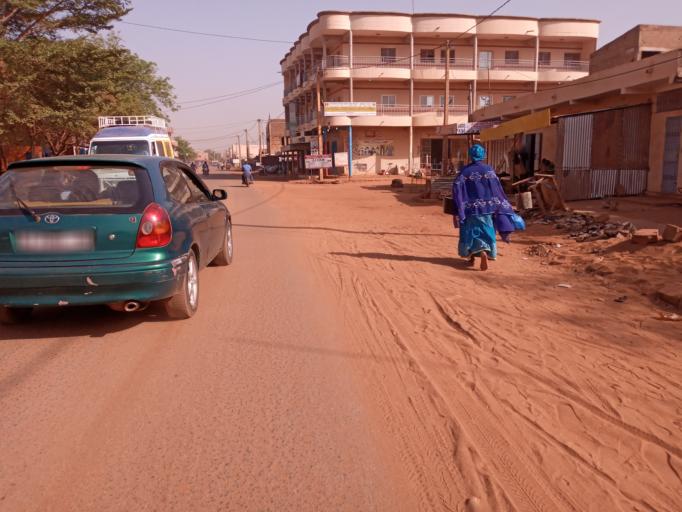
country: ML
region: Bamako
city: Bamako
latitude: 12.5828
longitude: -7.9582
